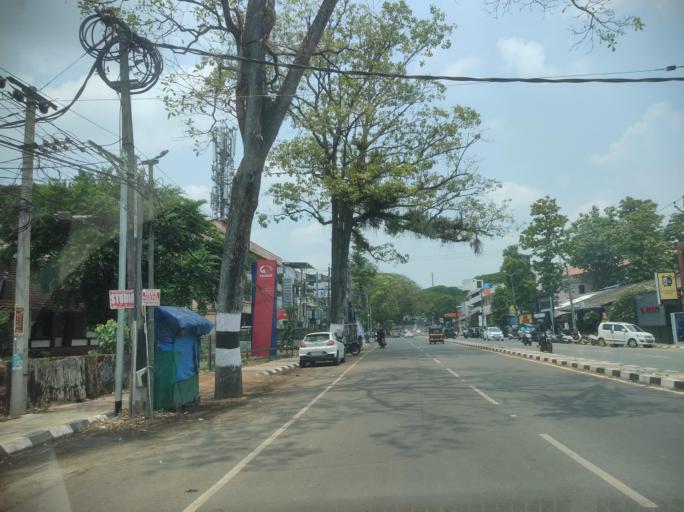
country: IN
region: Kerala
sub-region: Kottayam
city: Kottayam
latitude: 9.5921
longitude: 76.5273
